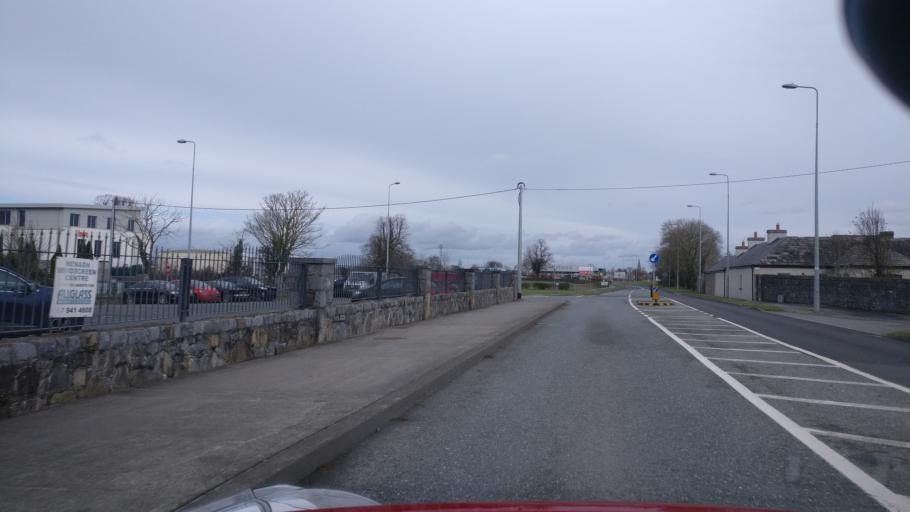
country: IE
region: Munster
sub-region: North Tipperary
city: Nenagh
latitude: 52.8591
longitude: -8.2244
